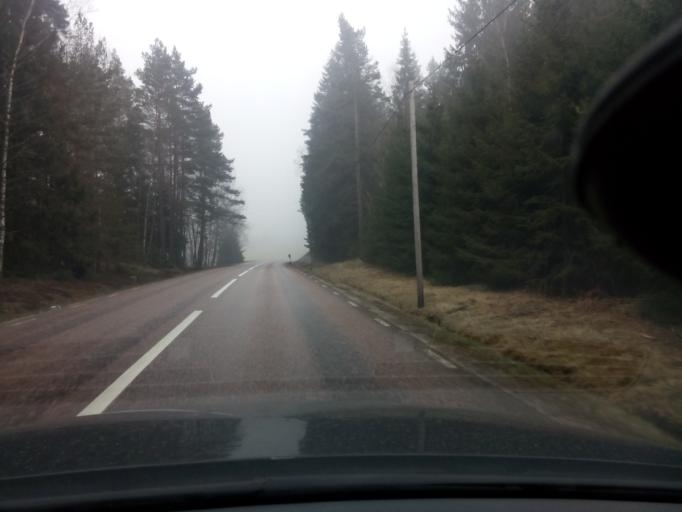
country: SE
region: Soedermanland
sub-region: Nykopings Kommun
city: Nykoping
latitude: 58.8408
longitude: 17.0673
